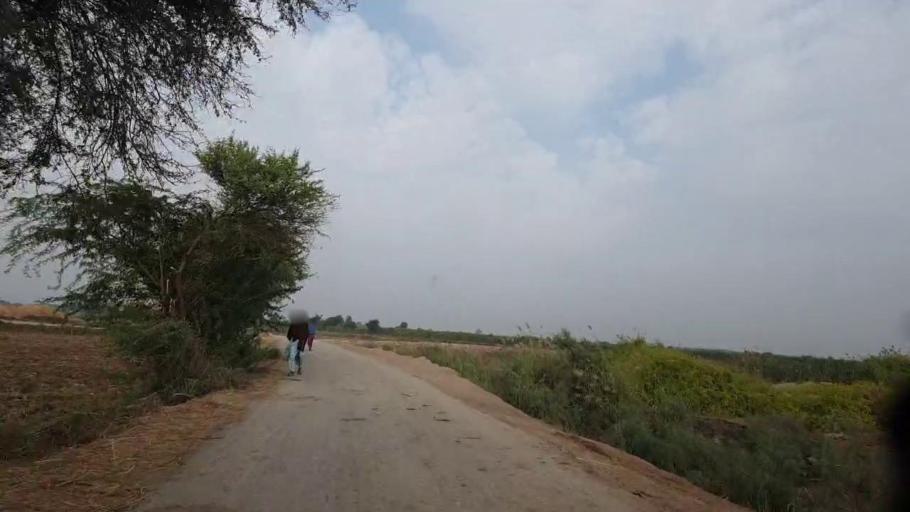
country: PK
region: Sindh
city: Tando Muhammad Khan
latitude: 25.0973
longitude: 68.4304
